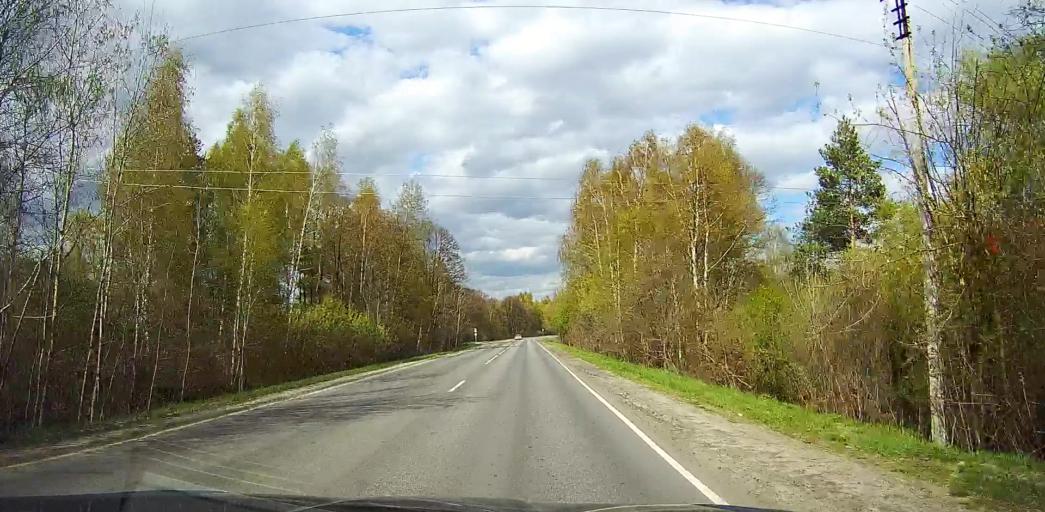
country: RU
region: Moskovskaya
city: Rakhmanovo
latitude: 55.7333
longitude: 38.6331
